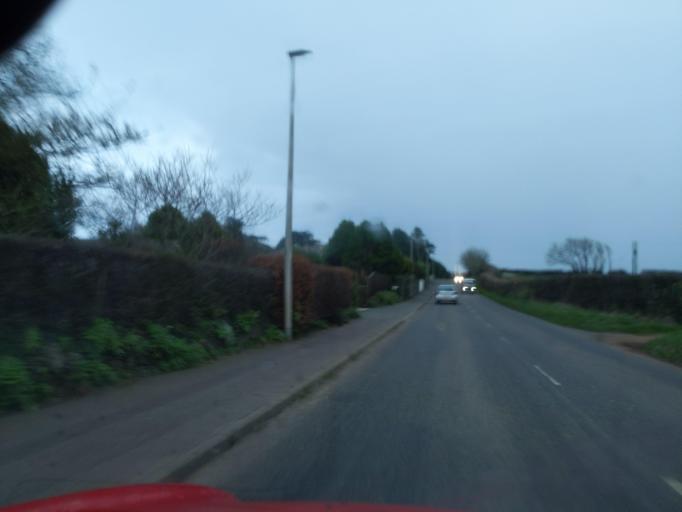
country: GB
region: England
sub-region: Devon
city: Wembury
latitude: 50.3408
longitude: -4.0741
